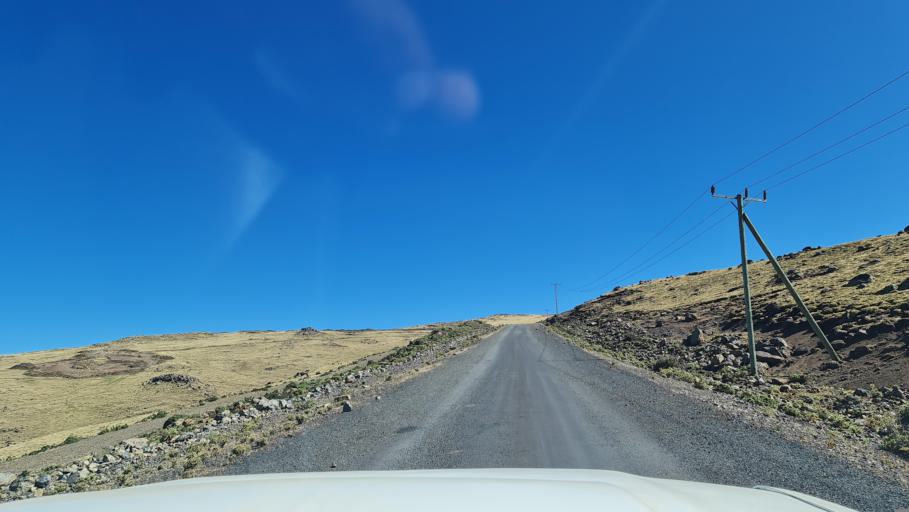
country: ET
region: Amhara
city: Debark'
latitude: 13.1432
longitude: 38.1794
